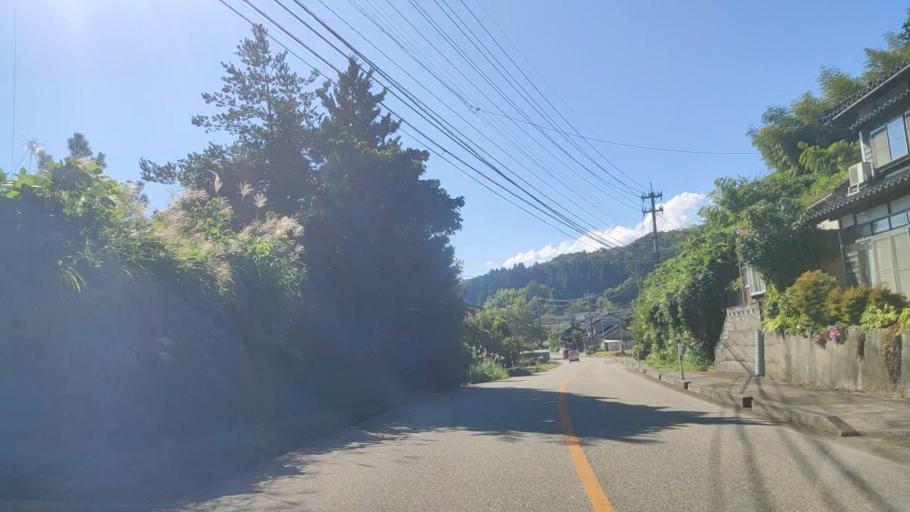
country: JP
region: Ishikawa
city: Nanao
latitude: 37.3373
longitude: 137.2143
